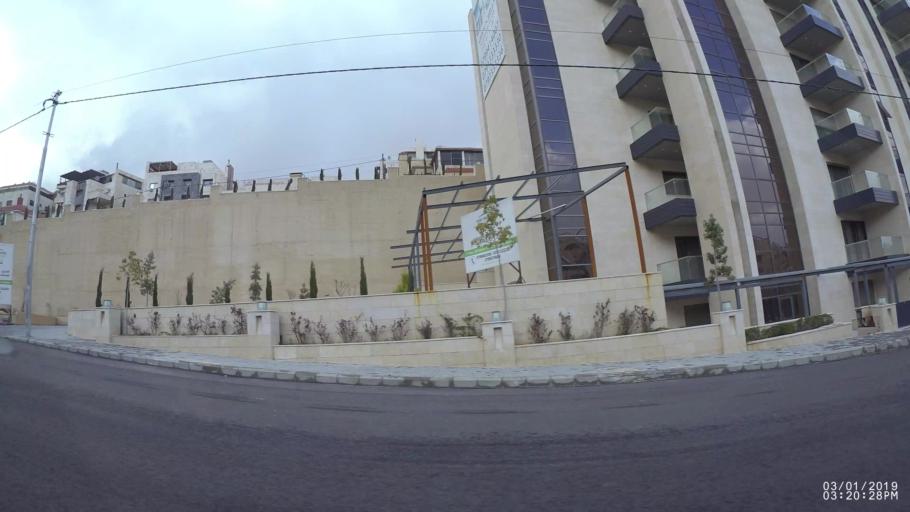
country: JO
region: Amman
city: Al Bunayyat ash Shamaliyah
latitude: 31.9433
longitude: 35.8925
